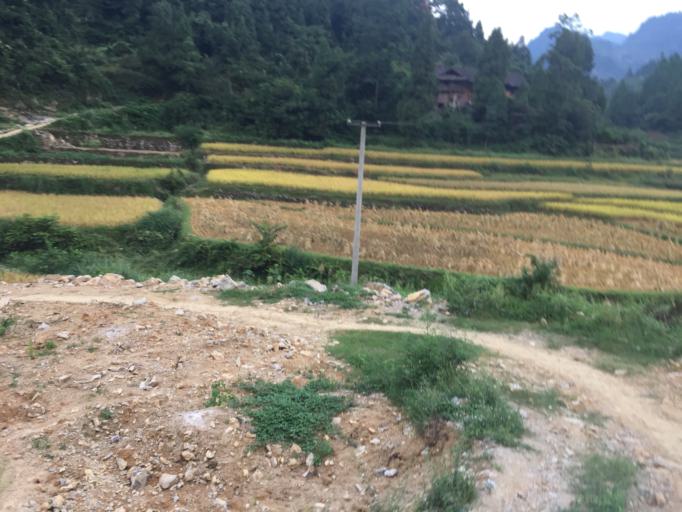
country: CN
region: Guizhou Sheng
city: Shiqian
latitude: 27.6074
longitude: 107.9947
